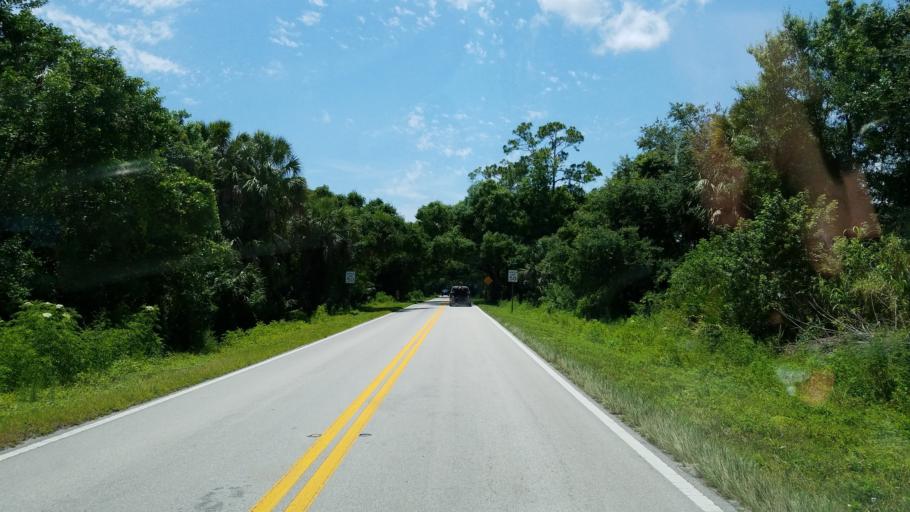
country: US
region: Florida
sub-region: Martin County
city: Indiantown
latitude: 27.1621
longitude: -80.5548
